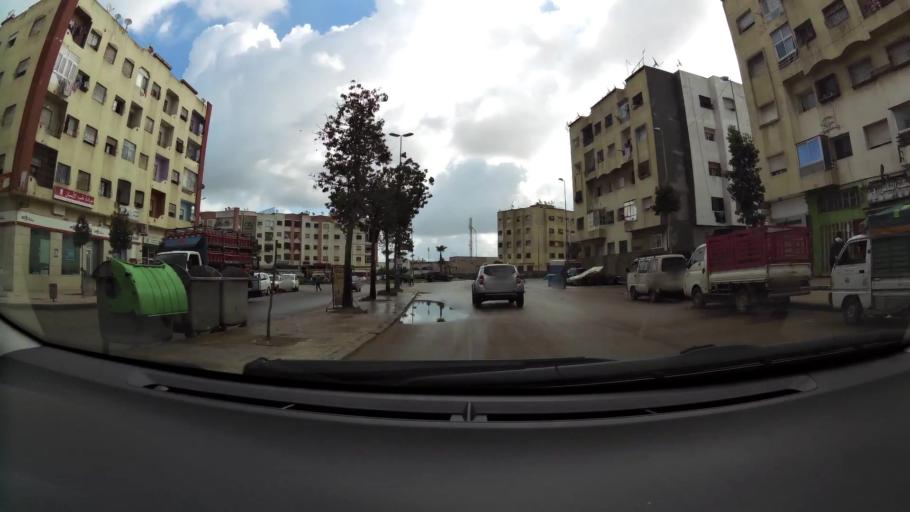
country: MA
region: Grand Casablanca
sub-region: Mediouna
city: Tit Mellil
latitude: 33.5909
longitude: -7.5174
